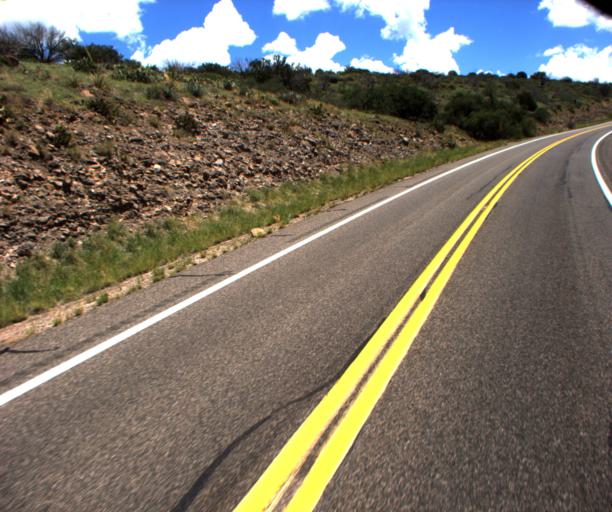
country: US
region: Arizona
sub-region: Yavapai County
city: Lake Montezuma
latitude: 34.4926
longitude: -111.7080
